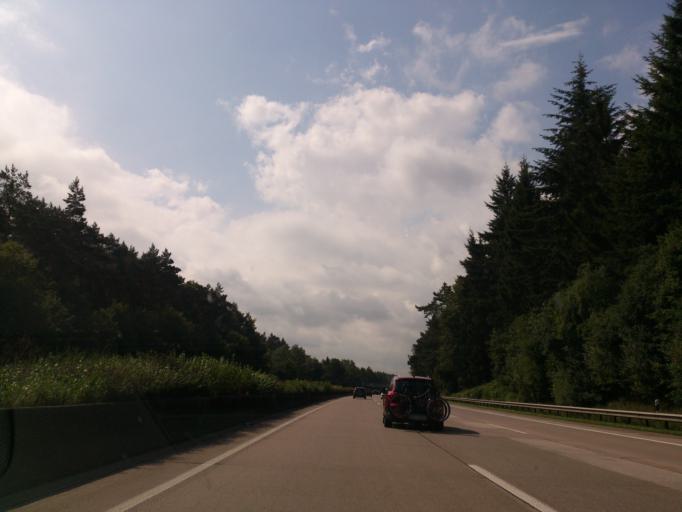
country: DE
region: Lower Saxony
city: Garlstorf
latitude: 53.2567
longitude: 10.0882
